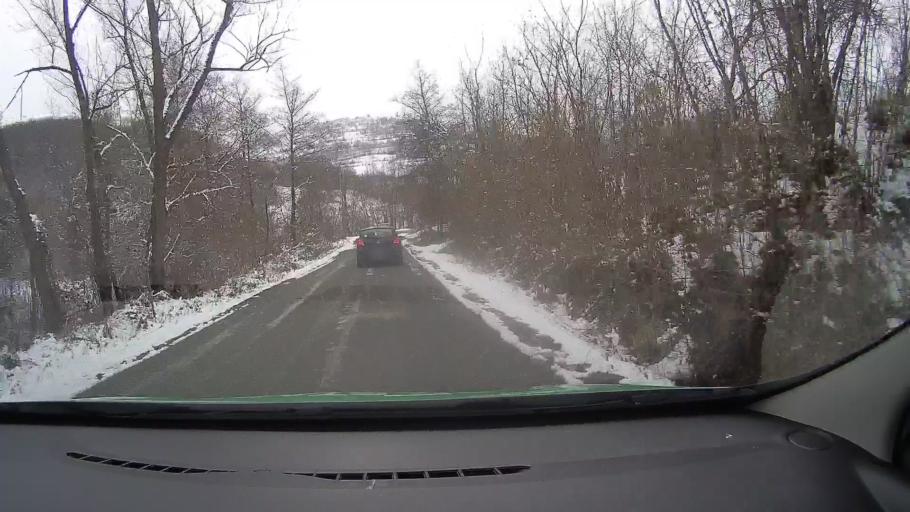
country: RO
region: Alba
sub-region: Comuna Almasu Mare
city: Almasu Mare
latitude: 46.0818
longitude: 23.1208
